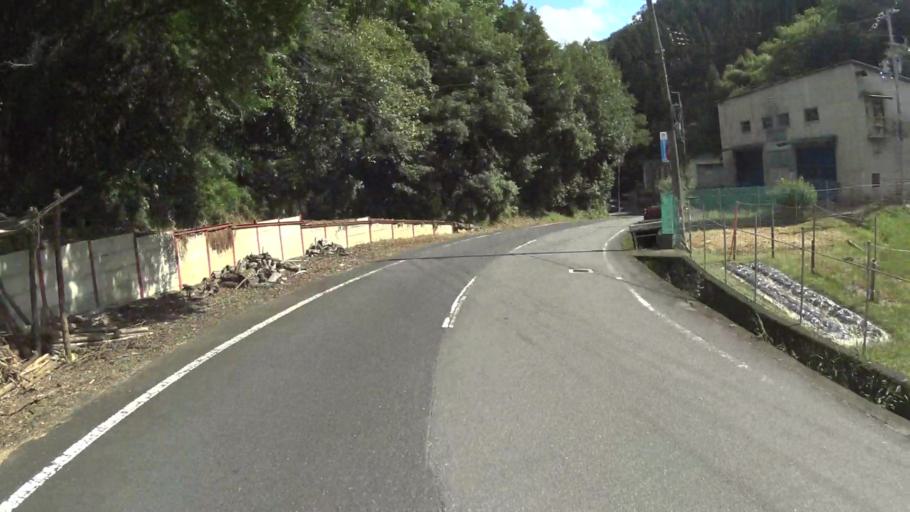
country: JP
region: Kyoto
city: Uji
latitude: 34.9109
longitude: 135.8619
